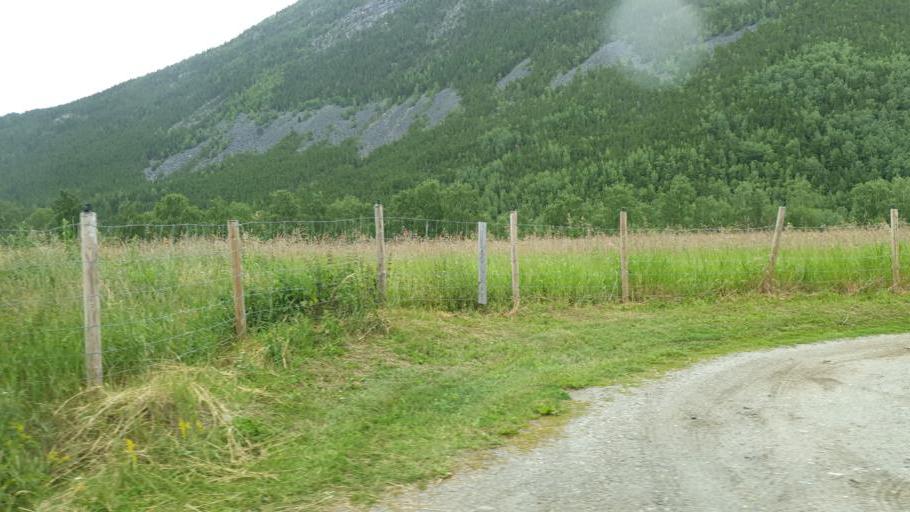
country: NO
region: Oppland
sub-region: Sel
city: Otta
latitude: 61.8499
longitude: 9.4186
